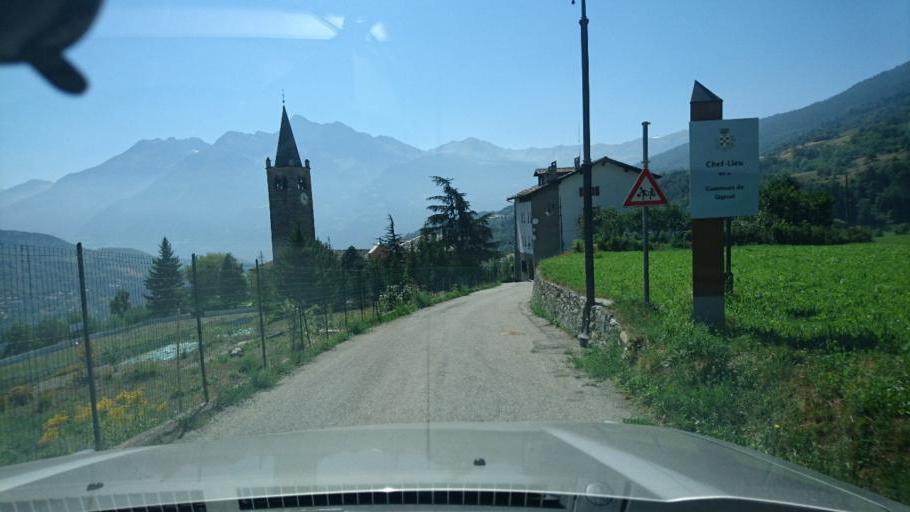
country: IT
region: Aosta Valley
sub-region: Valle d'Aosta
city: Gignod
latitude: 45.7828
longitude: 7.2967
